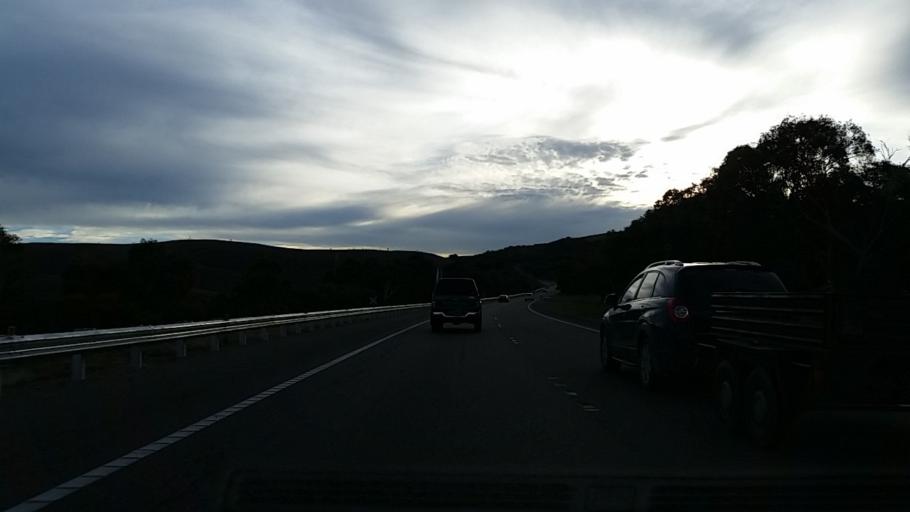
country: AU
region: South Australia
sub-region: Mount Barker
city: Callington
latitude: -35.1150
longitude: 138.9917
